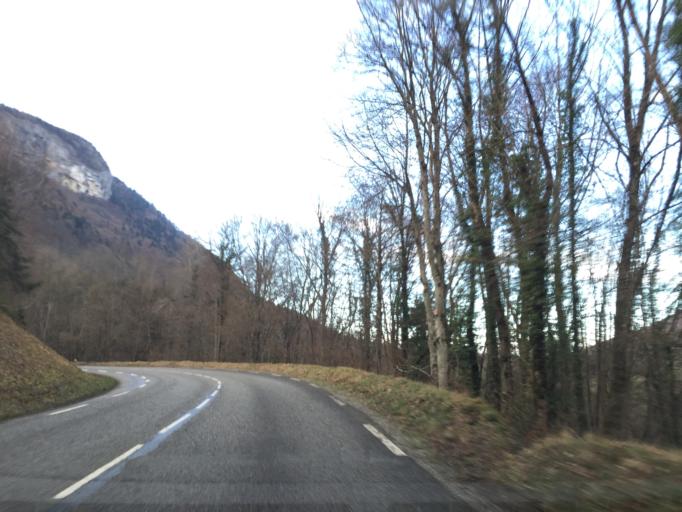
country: FR
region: Rhone-Alpes
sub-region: Departement de la Haute-Savoie
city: Gruffy
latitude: 45.7479
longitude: 6.0744
